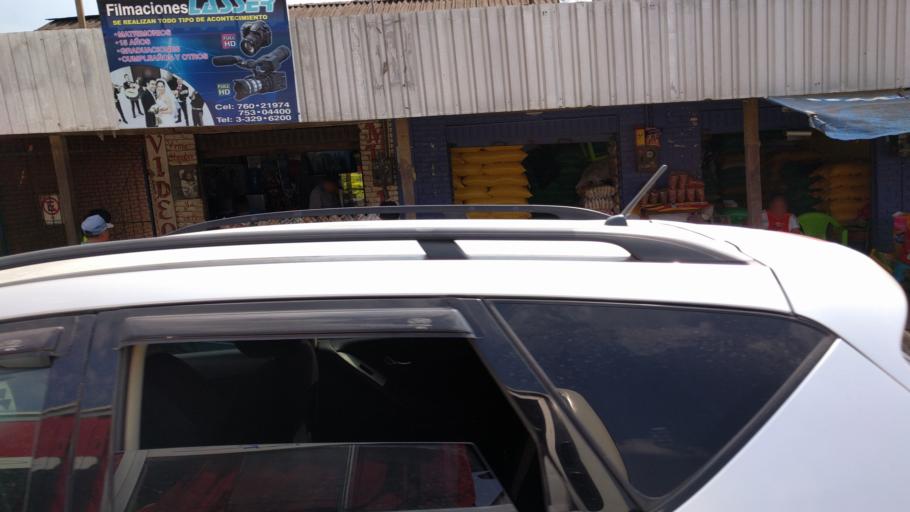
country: BO
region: Santa Cruz
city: Santiago del Torno
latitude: -17.9932
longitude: -63.3833
